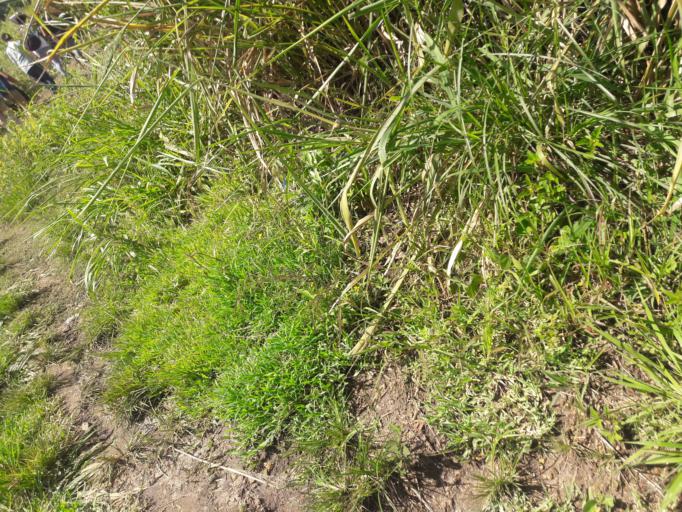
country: GT
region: Guatemala
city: Amatitlan
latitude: 14.4636
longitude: -90.5774
